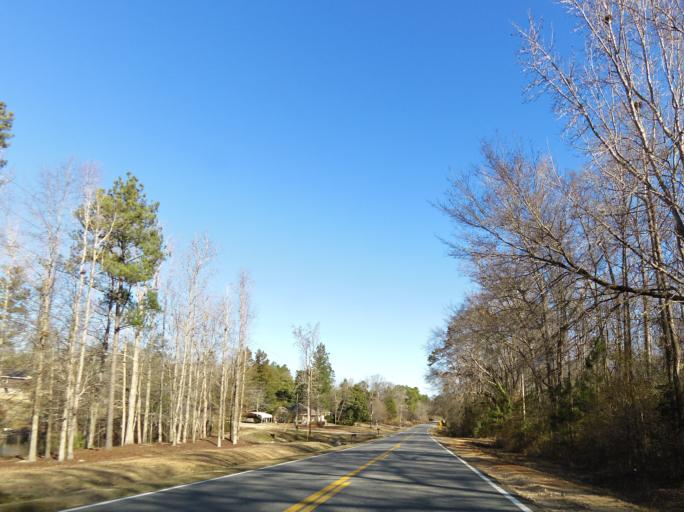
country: US
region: Georgia
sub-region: Bibb County
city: West Point
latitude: 32.7636
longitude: -83.7592
